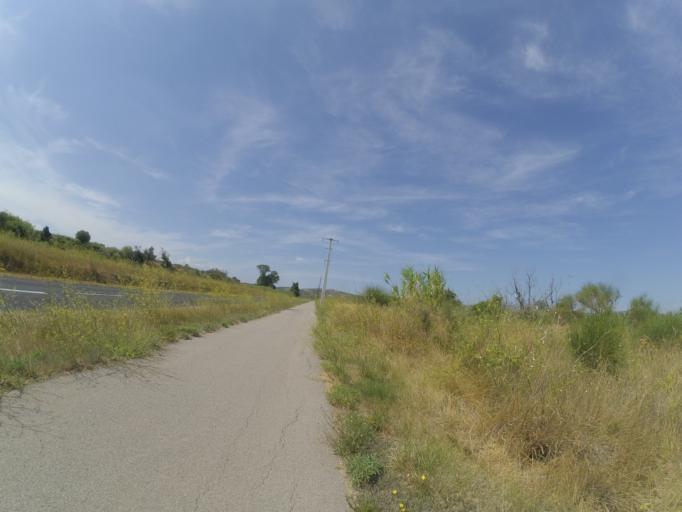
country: FR
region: Languedoc-Roussillon
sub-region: Departement des Pyrenees-Orientales
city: Peyrestortes
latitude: 42.7560
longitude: 2.8398
